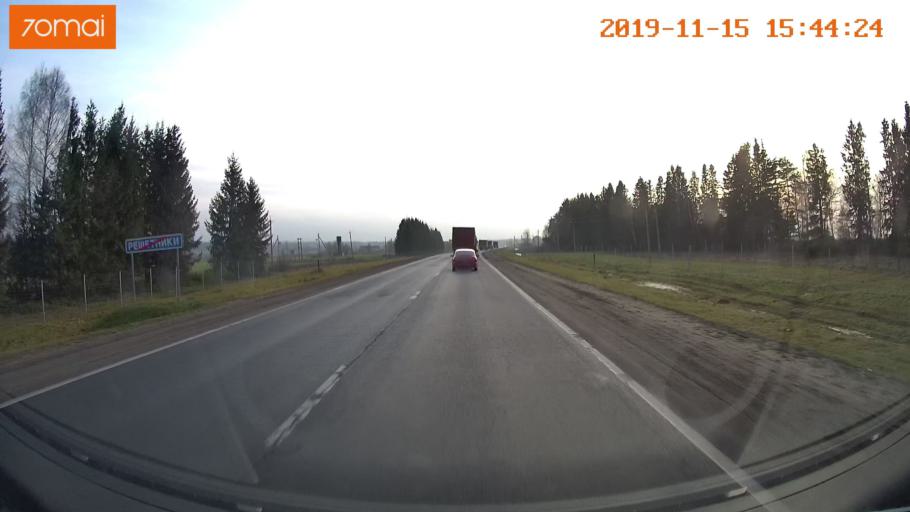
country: RU
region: Jaroslavl
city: Danilov
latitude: 57.9706
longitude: 40.0223
